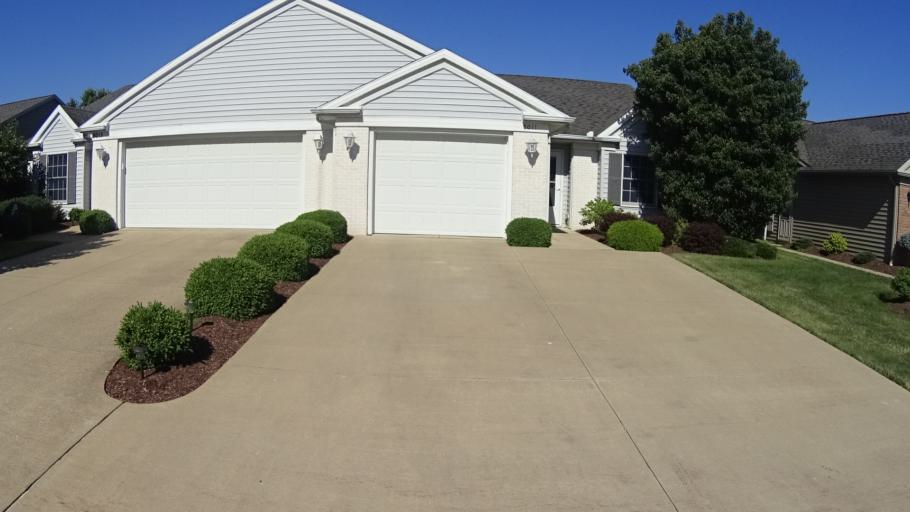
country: US
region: Ohio
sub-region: Erie County
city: Sandusky
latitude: 41.3929
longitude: -82.6455
